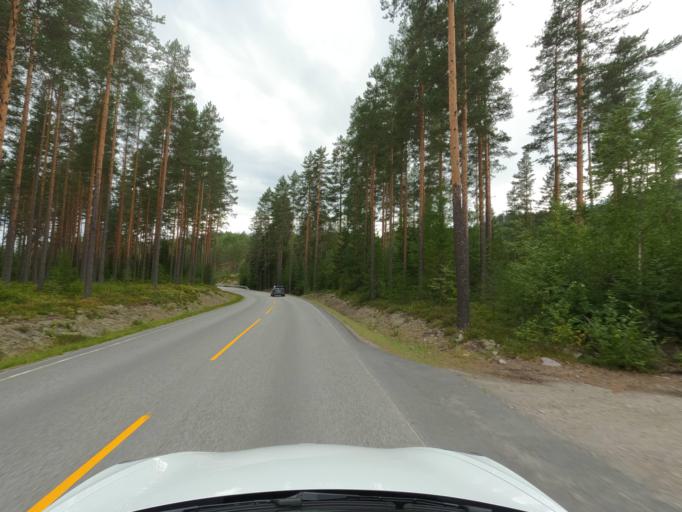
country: NO
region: Telemark
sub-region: Hjartdal
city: Sauland
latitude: 59.7114
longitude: 9.0132
